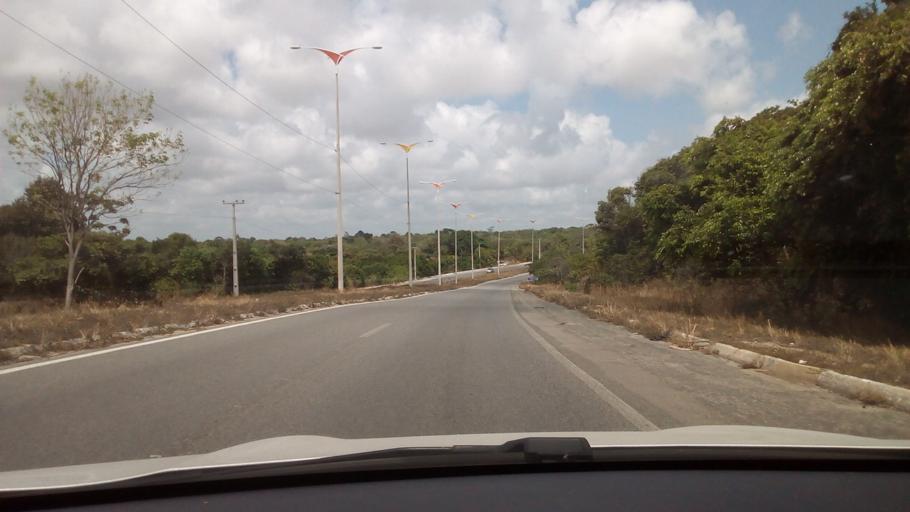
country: BR
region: Paraiba
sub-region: Joao Pessoa
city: Joao Pessoa
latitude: -7.1831
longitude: -34.8048
